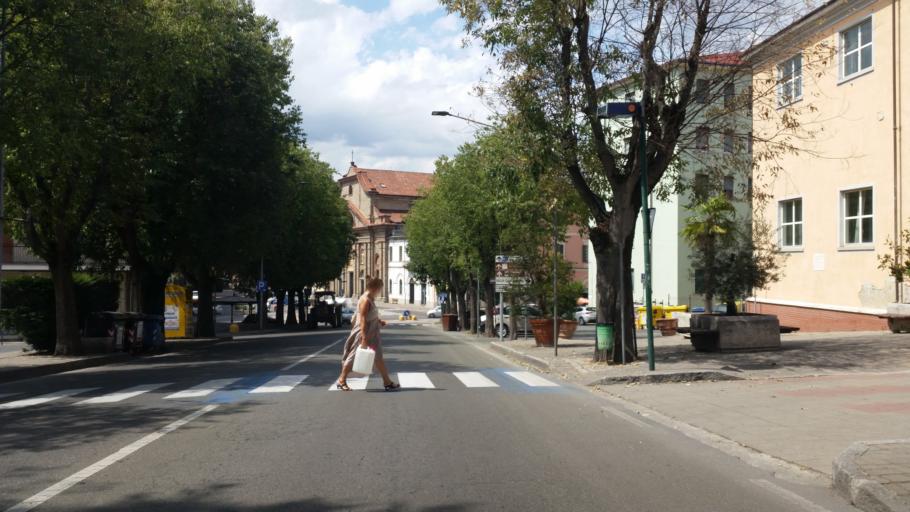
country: IT
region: Piedmont
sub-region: Provincia di Alessandria
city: Acqui Terme
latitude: 44.6761
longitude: 8.4717
